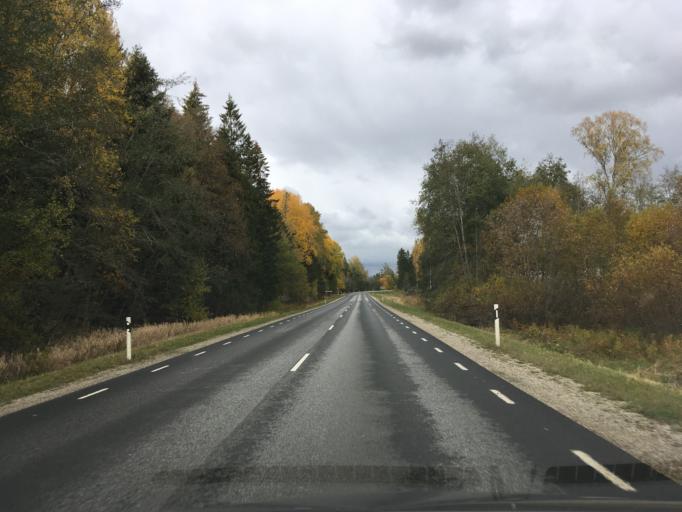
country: EE
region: Harju
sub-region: Anija vald
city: Kehra
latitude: 59.2972
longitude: 25.3675
